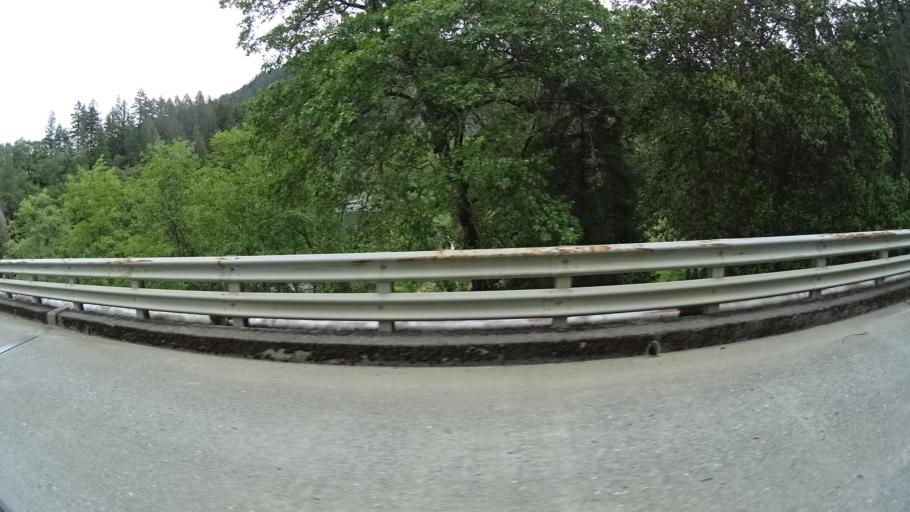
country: US
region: California
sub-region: Humboldt County
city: Willow Creek
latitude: 40.9452
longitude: -123.6238
